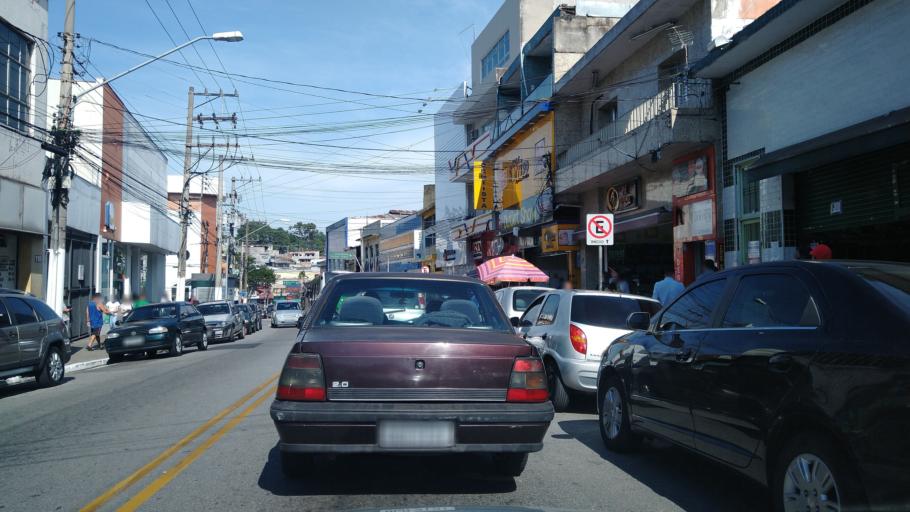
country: BR
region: Sao Paulo
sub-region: Sao Paulo
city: Sao Paulo
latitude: -23.4727
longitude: -46.6669
